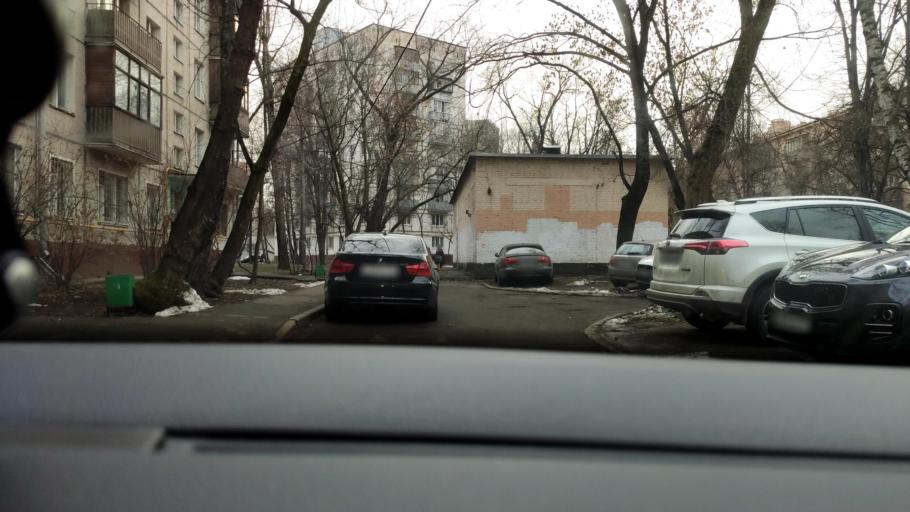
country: RU
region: Moscow
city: Novokuz'minki
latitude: 55.7126
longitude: 37.7725
